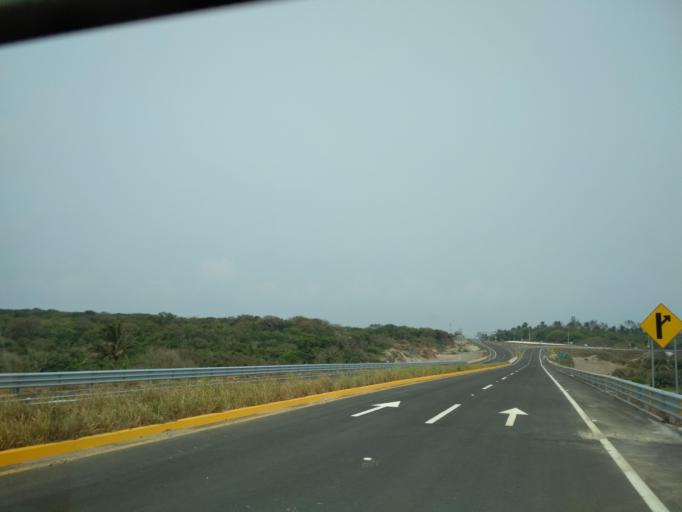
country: MX
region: Veracruz
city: Anton Lizardo
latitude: 19.0503
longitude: -96.0045
